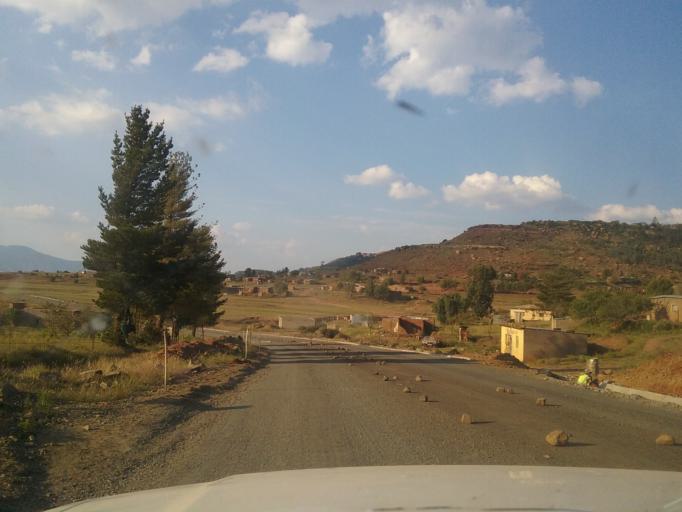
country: LS
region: Quthing
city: Quthing
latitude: -30.4218
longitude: 27.5967
